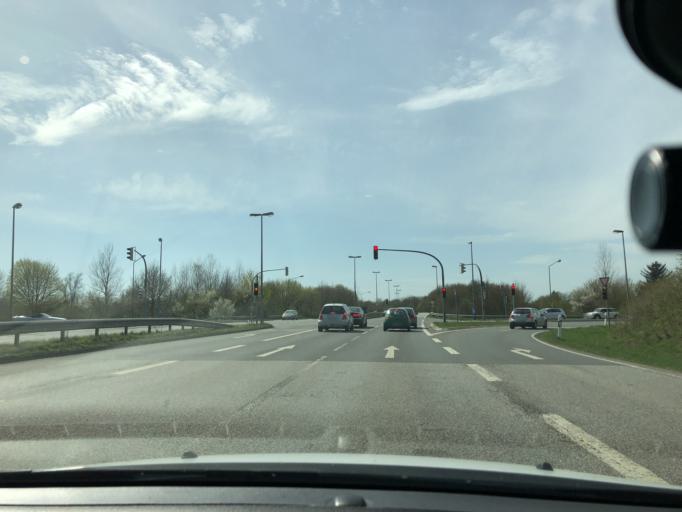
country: DE
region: Schleswig-Holstein
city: Flensburg
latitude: 54.7617
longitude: 9.4518
